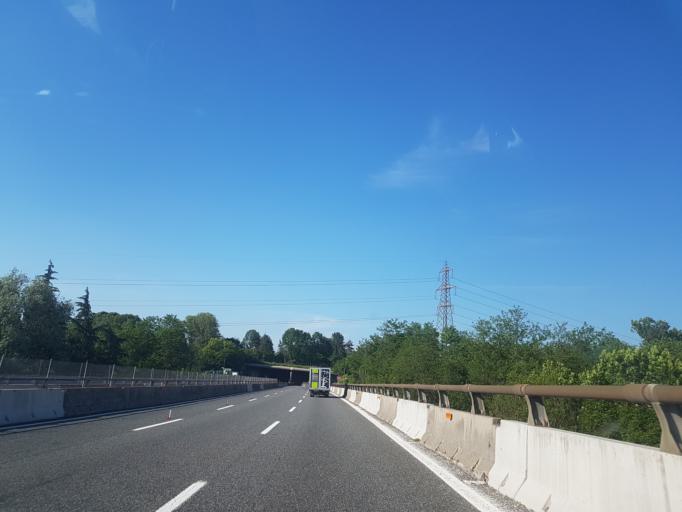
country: IT
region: Lombardy
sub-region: Provincia di Varese
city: Golasecca
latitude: 45.7039
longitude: 8.6470
